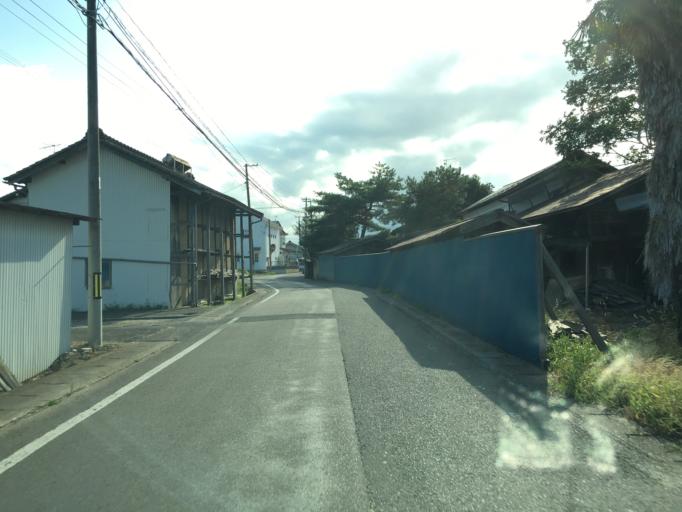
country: JP
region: Fukushima
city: Hobaramachi
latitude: 37.8254
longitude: 140.5684
